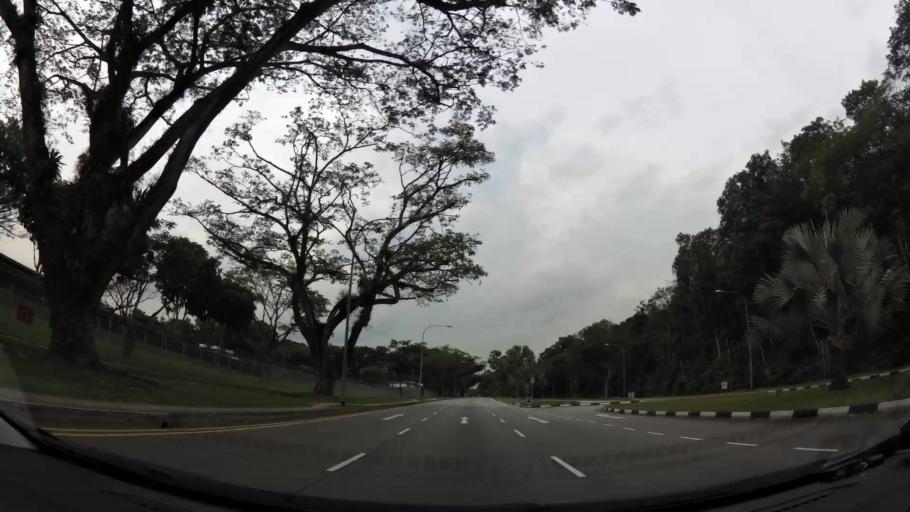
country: MY
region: Johor
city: Johor Bahru
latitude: 1.4077
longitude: 103.8205
